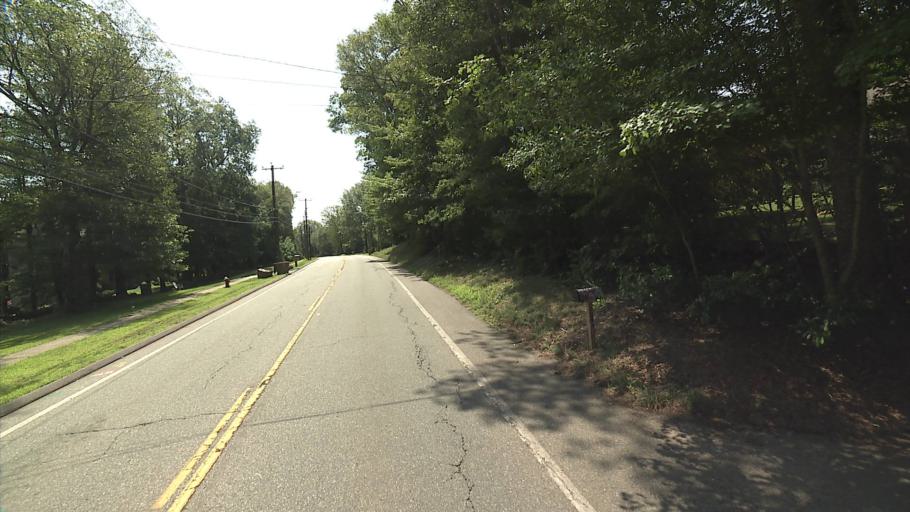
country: US
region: Connecticut
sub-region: New London County
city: Niantic
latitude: 41.3852
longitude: -72.2207
